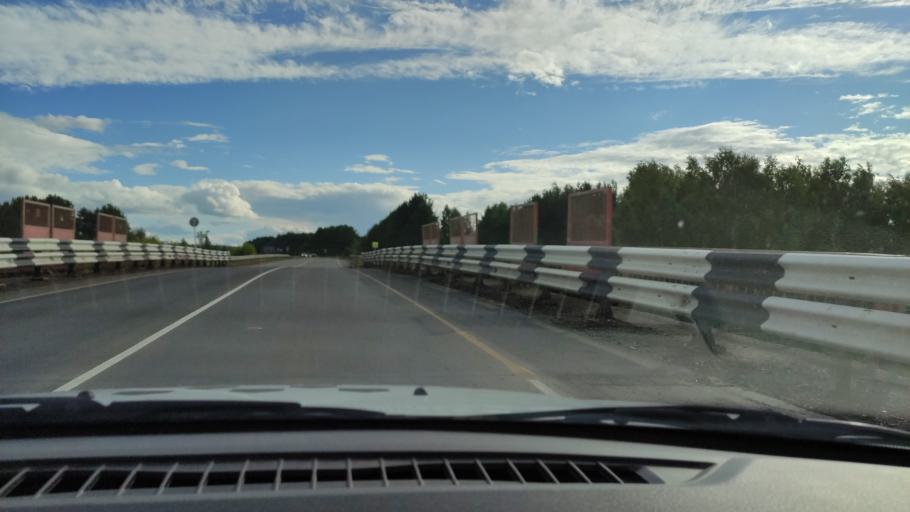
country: RU
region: Perm
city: Kungur
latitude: 57.4218
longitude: 56.9240
